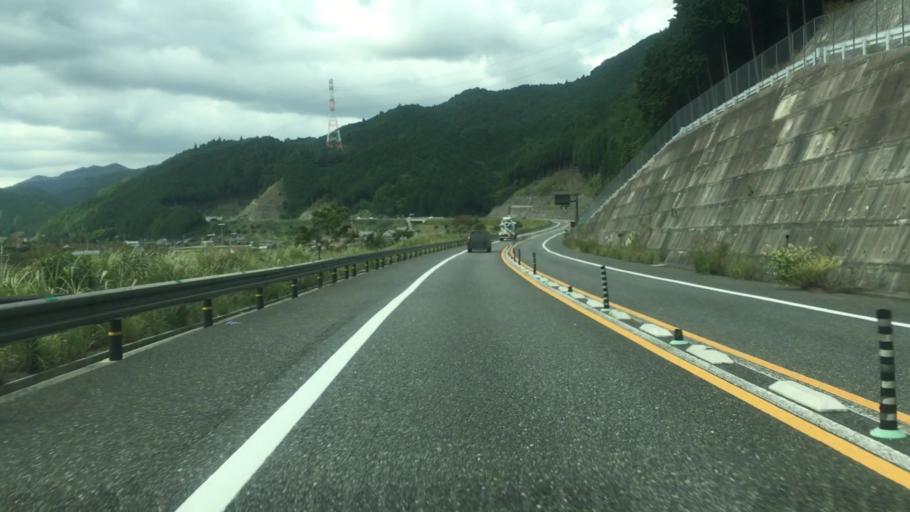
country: JP
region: Kyoto
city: Fukuchiyama
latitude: 35.2800
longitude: 134.9870
